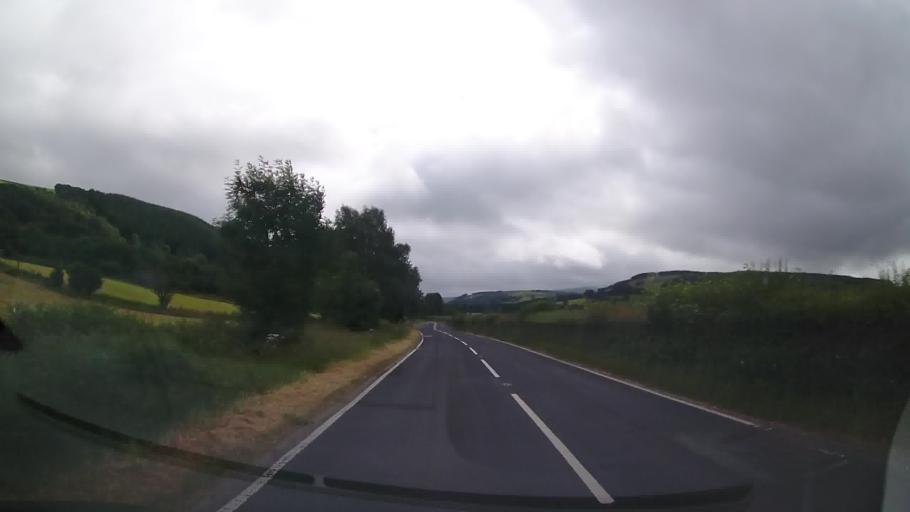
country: GB
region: Wales
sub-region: Denbighshire
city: Llandrillo
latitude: 52.9287
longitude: -3.4304
